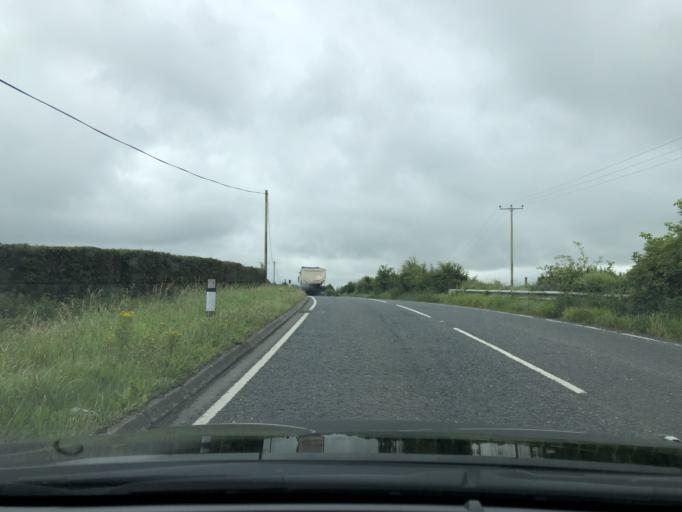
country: GB
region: Northern Ireland
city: Ballynahinch
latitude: 54.3581
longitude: -5.8575
